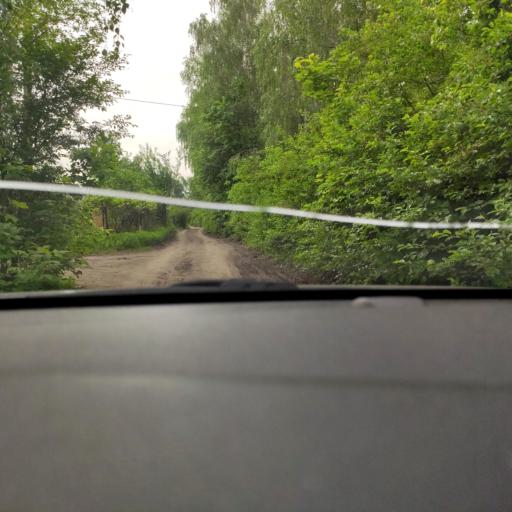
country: RU
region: Voronezj
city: Maslovka
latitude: 51.5937
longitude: 39.1663
